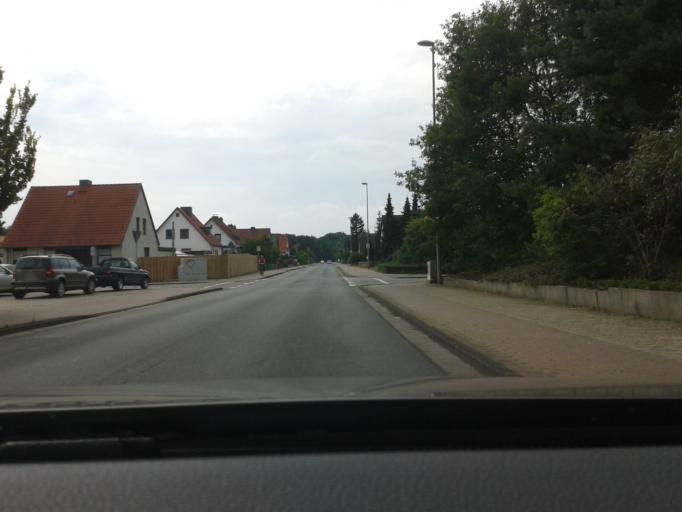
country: DE
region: Lower Saxony
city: Gifhorn
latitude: 52.4834
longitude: 10.5618
